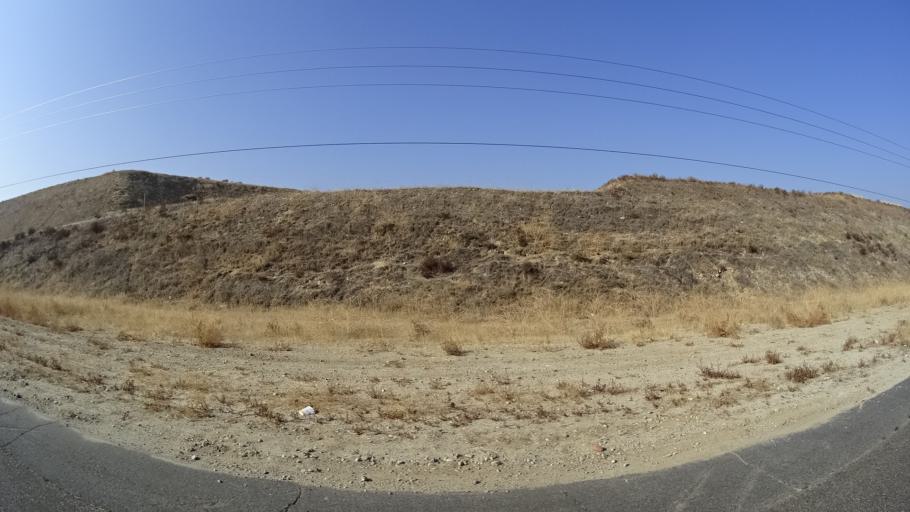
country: US
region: California
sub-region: Kern County
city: Oildale
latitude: 35.4142
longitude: -118.8596
